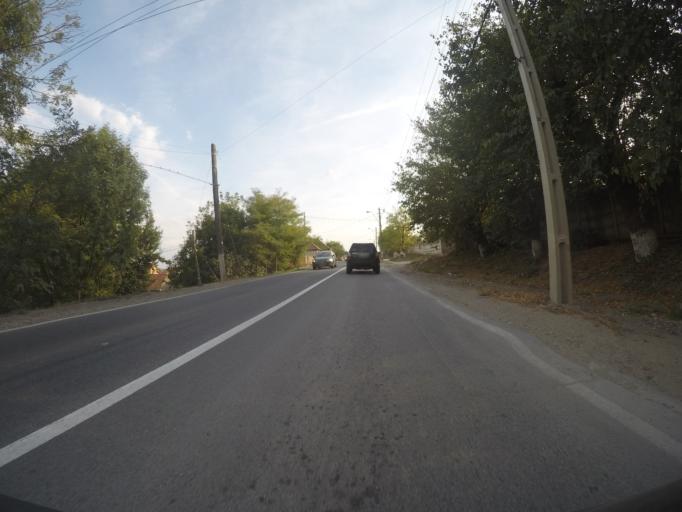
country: RO
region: Alba
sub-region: Oras Teius
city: Teius
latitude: 46.2132
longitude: 23.6774
